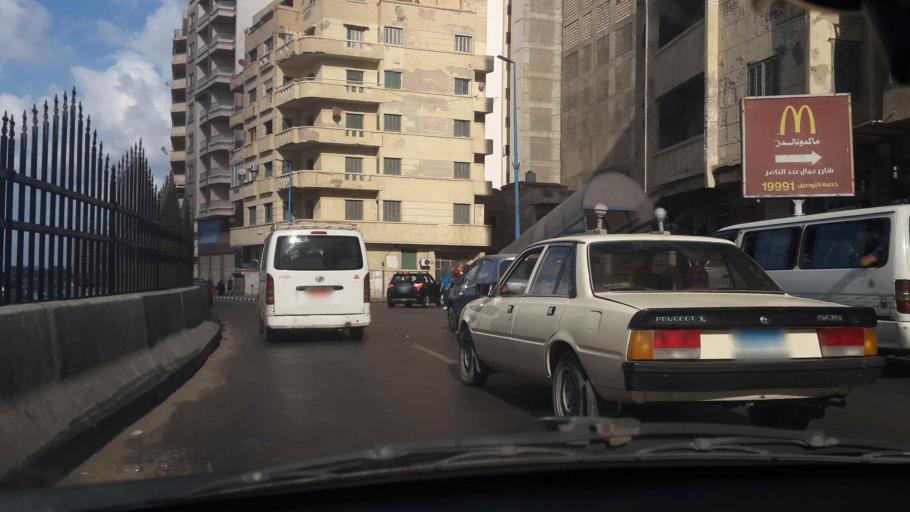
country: EG
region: Alexandria
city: Alexandria
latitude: 31.2699
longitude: 29.9932
